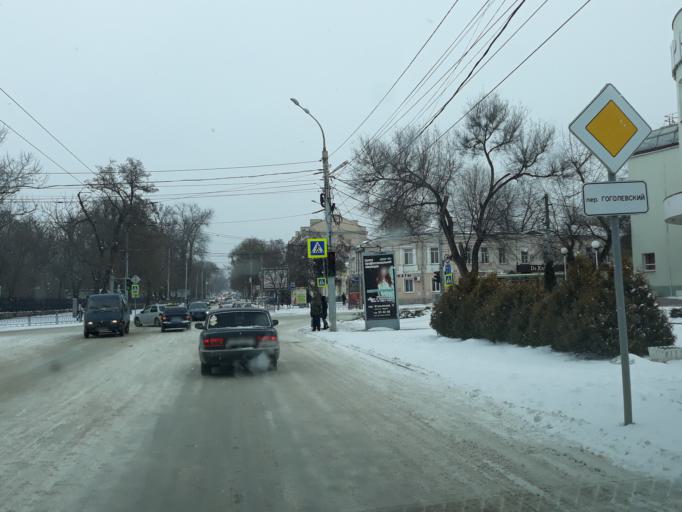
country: RU
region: Rostov
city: Taganrog
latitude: 47.2207
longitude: 38.9209
